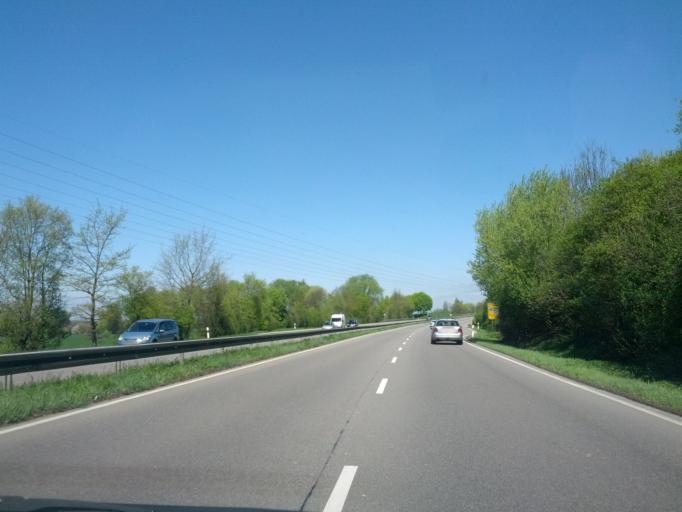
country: DE
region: Baden-Wuerttemberg
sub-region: Freiburg Region
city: Umkirch
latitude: 48.0032
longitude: 7.7990
